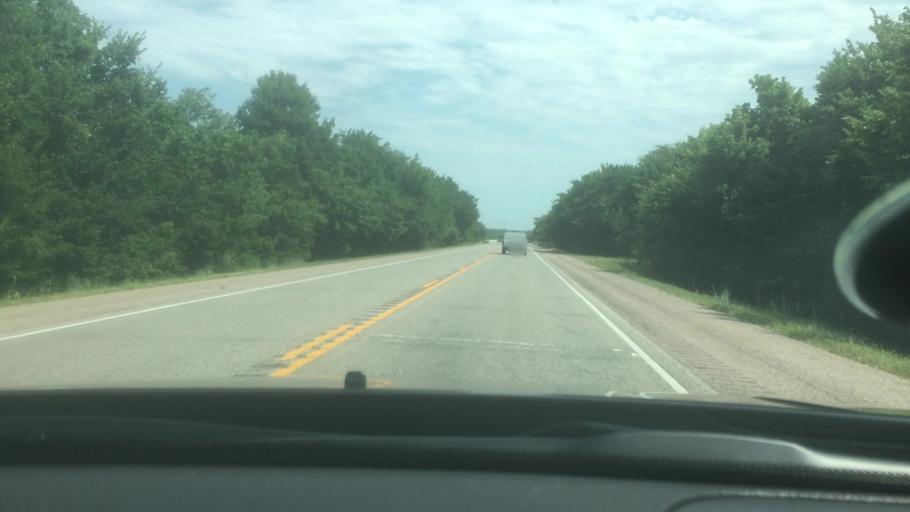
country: US
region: Oklahoma
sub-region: Seminole County
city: Maud
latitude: 35.0793
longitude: -96.9313
